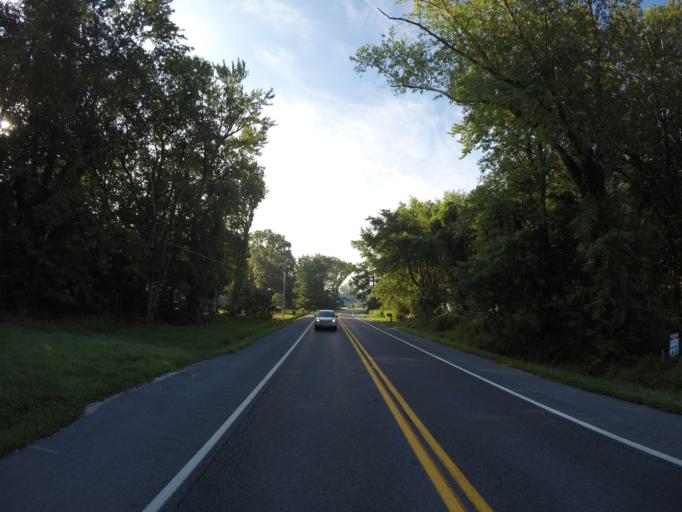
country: US
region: Delaware
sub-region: Sussex County
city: Selbyville
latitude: 38.5003
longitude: -75.1729
